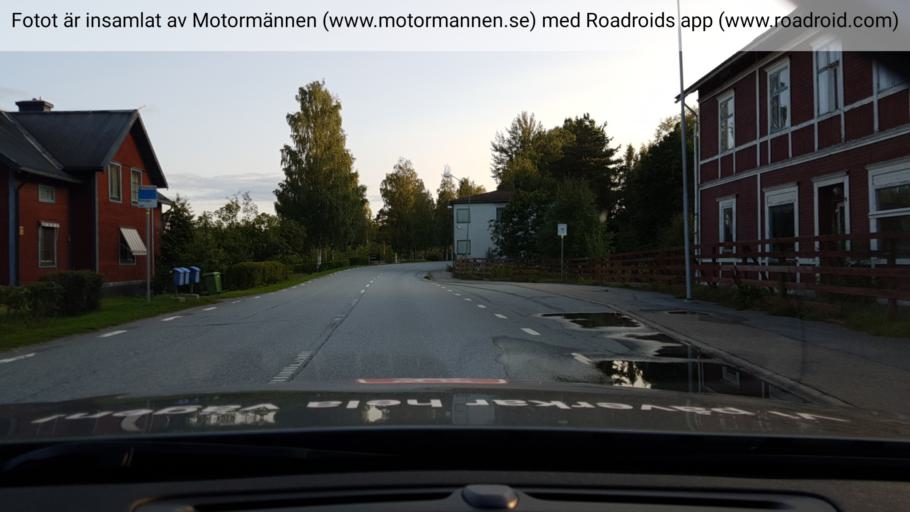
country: SE
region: OErebro
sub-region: Ljusnarsbergs Kommun
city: Kopparberg
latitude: 59.8811
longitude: 15.0059
